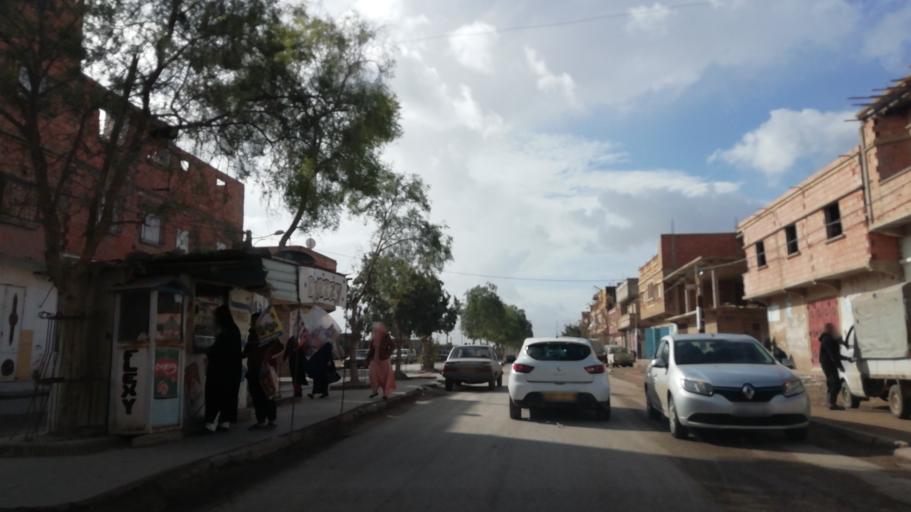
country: DZ
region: Oran
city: Es Senia
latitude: 35.6390
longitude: -0.5754
